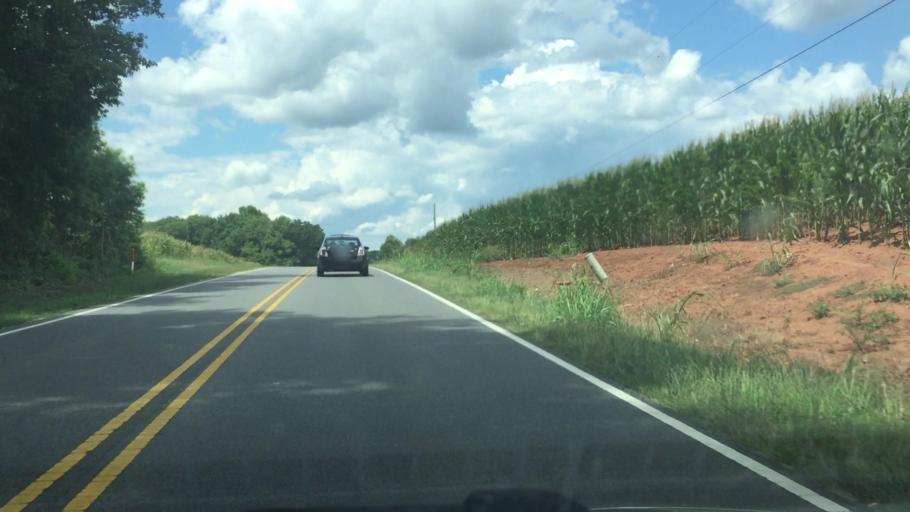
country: US
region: North Carolina
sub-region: Rowan County
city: Enochville
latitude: 35.4841
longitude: -80.7048
